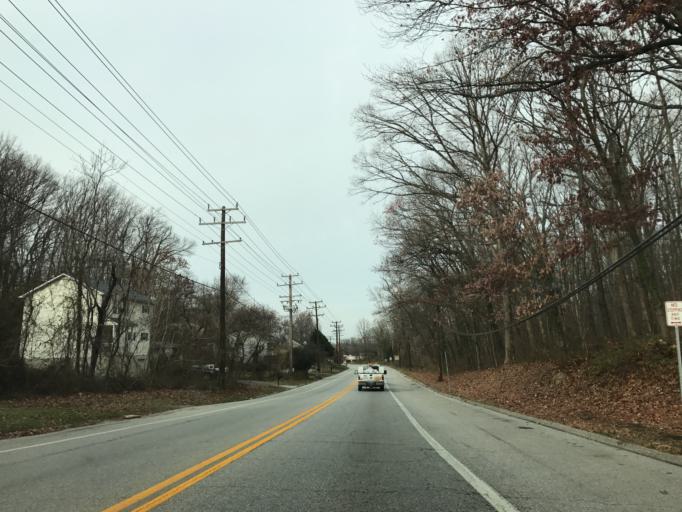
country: US
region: Maryland
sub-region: Anne Arundel County
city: Pumphrey
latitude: 39.2111
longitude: -76.6424
